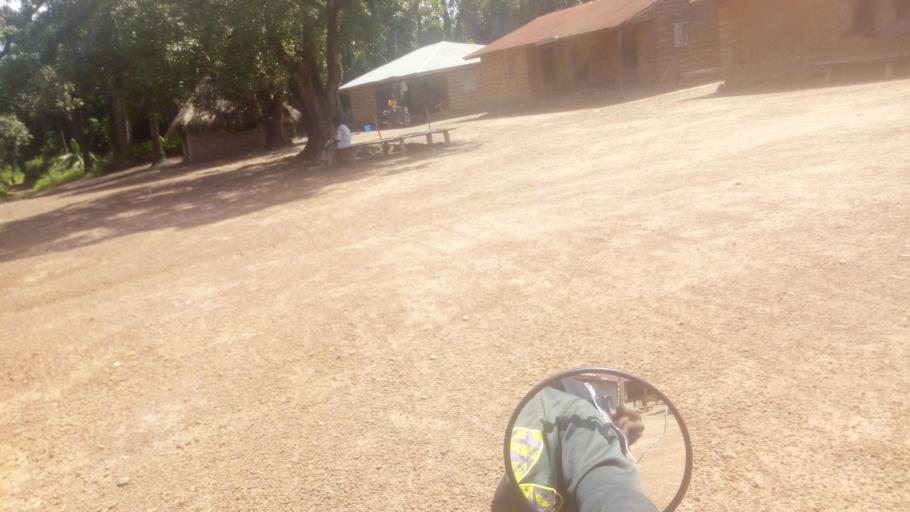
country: SL
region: Northern Province
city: Magburaka
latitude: 8.6397
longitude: -12.0603
